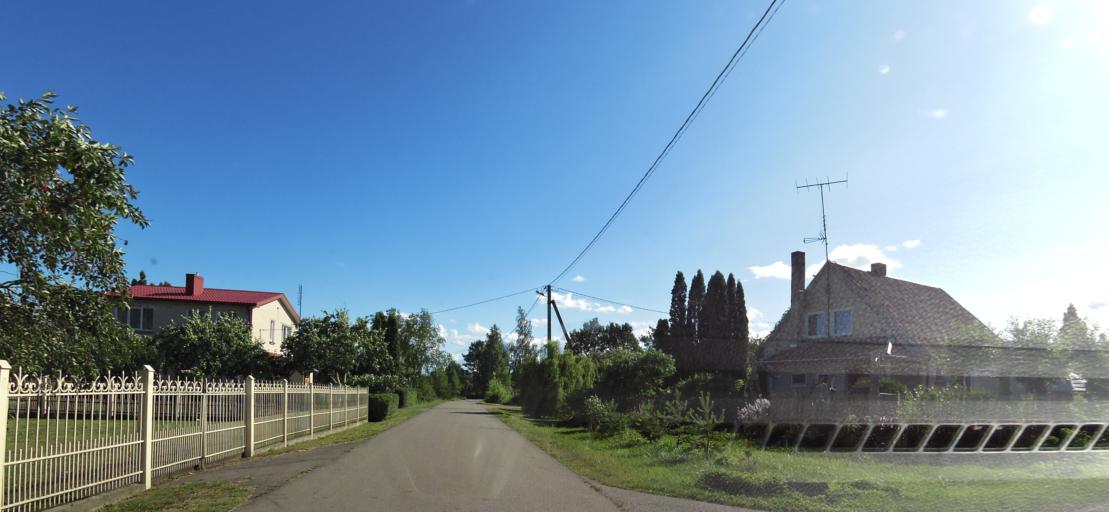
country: LT
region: Panevezys
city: Pasvalys
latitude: 56.1551
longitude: 24.4447
